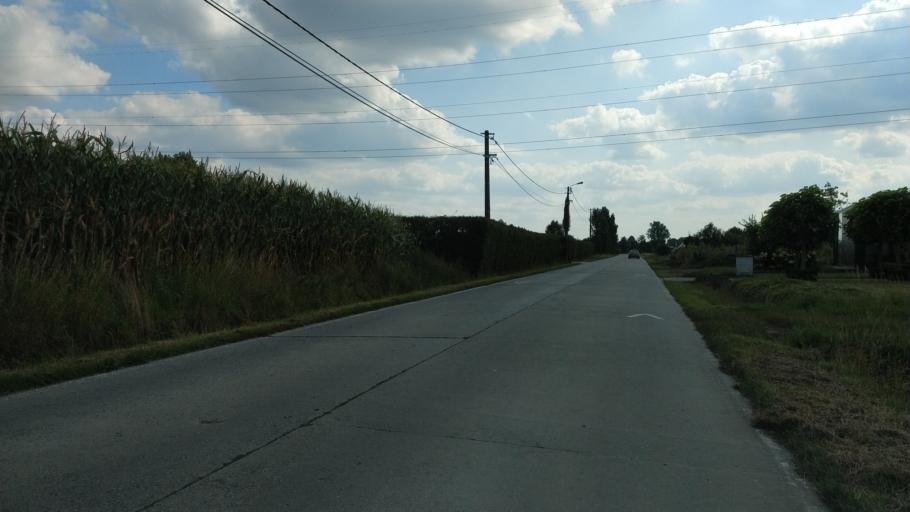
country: BE
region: Flanders
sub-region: Provincie Oost-Vlaanderen
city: Evergem
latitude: 51.1469
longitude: 3.6950
